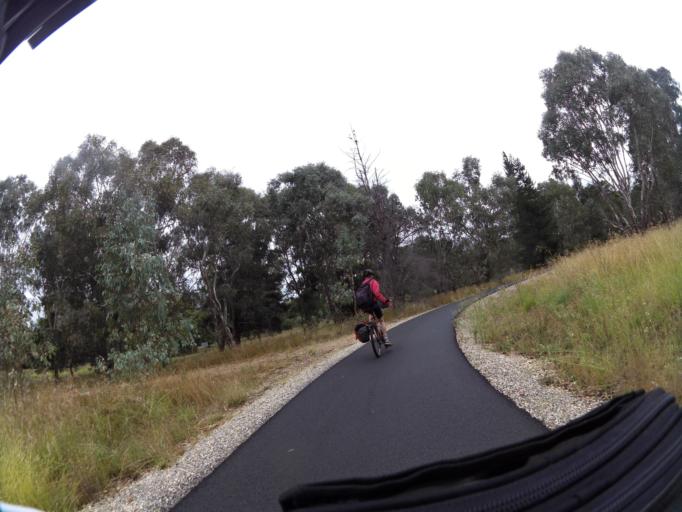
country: AU
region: Victoria
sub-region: Wodonga
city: Wodonga
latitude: -36.1485
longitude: 146.9279
